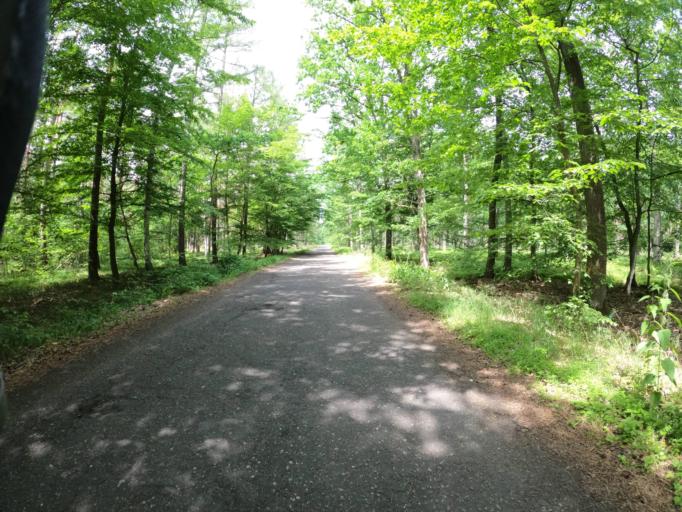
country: PL
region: West Pomeranian Voivodeship
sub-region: Powiat mysliborski
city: Boleszkowice
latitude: 52.7019
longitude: 14.5118
